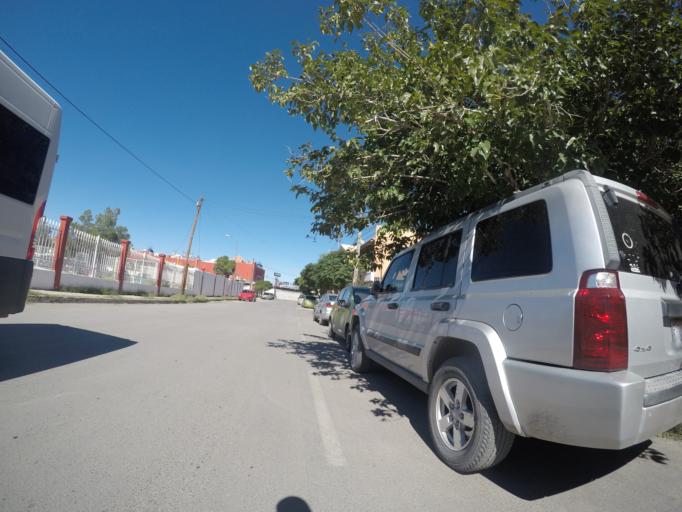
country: MX
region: Chihuahua
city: Ciudad Juarez
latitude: 31.7204
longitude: -106.4186
